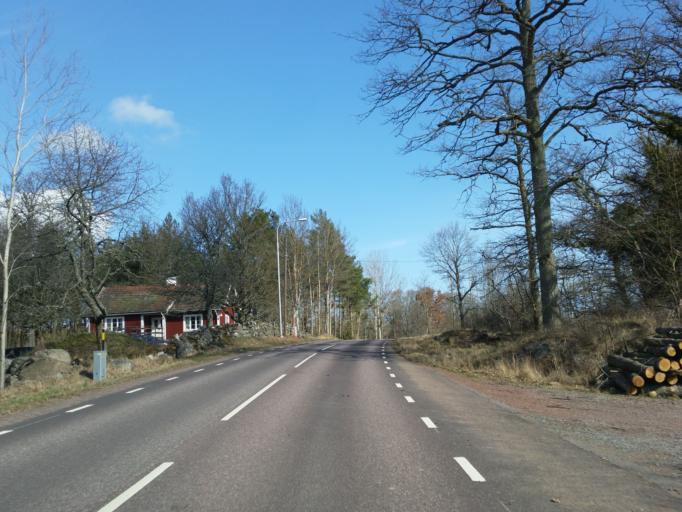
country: SE
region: Kalmar
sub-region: Monsteras Kommun
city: Timmernabben
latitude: 56.8625
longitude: 16.4088
